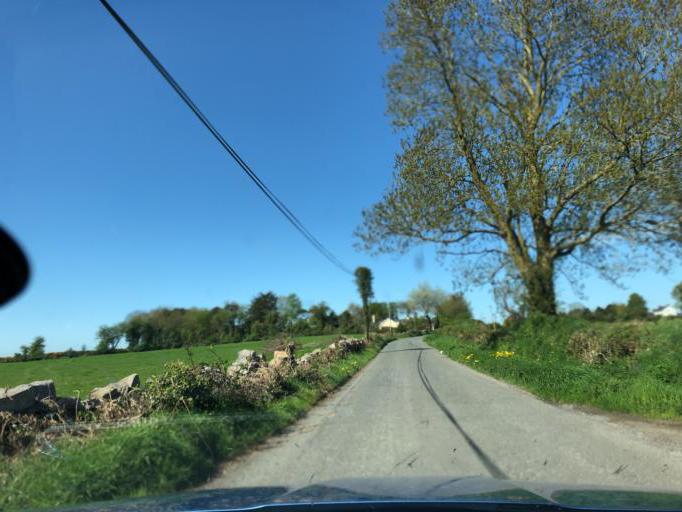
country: IE
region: Connaught
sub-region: County Galway
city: Portumna
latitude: 53.1789
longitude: -8.1819
